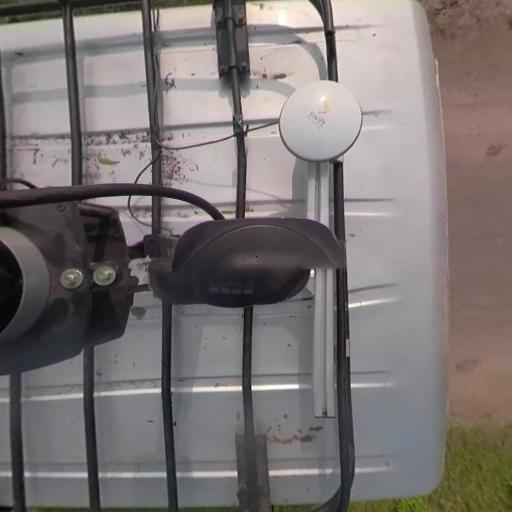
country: IN
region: Telangana
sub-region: Nalgonda
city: Suriapet
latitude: 17.1983
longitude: 79.4913
